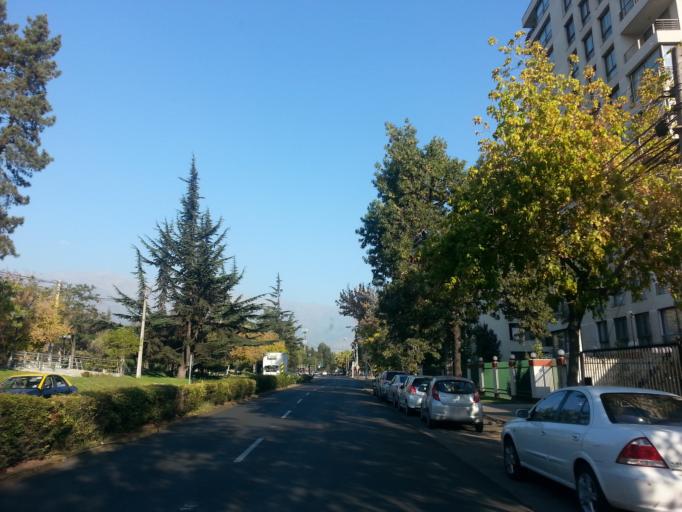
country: CL
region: Santiago Metropolitan
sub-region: Provincia de Santiago
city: Villa Presidente Frei, Nunoa, Santiago, Chile
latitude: -33.4293
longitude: -70.5875
